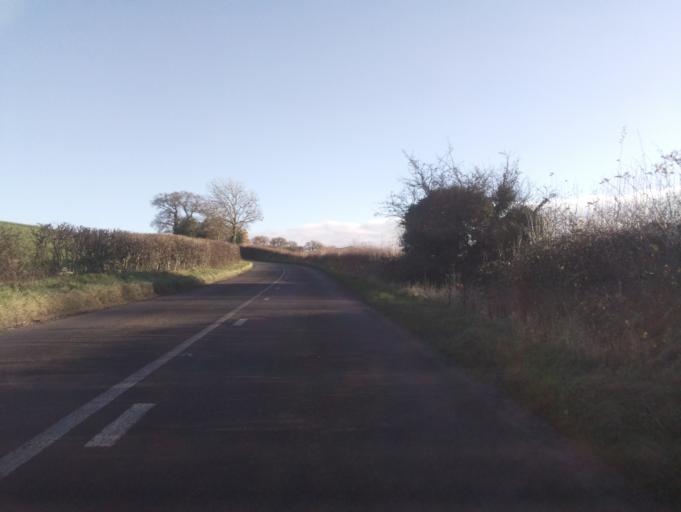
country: GB
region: England
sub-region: Staffordshire
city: Barton under Needwood
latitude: 52.8190
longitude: -1.7748
